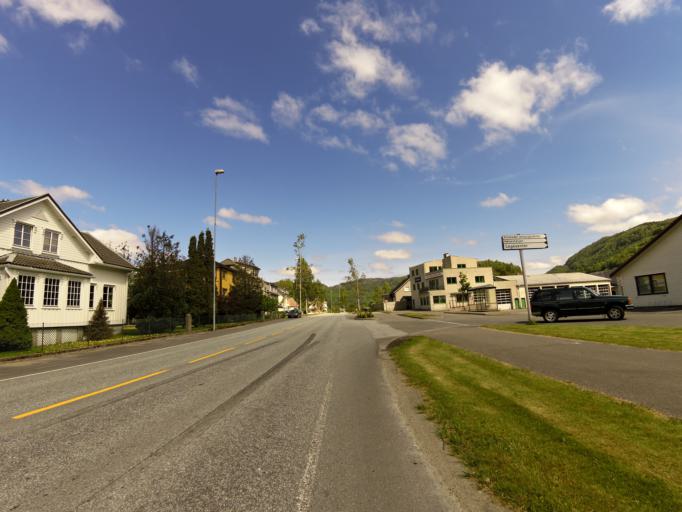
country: NO
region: Vest-Agder
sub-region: Kvinesdal
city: Liknes
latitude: 58.3099
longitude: 6.9583
